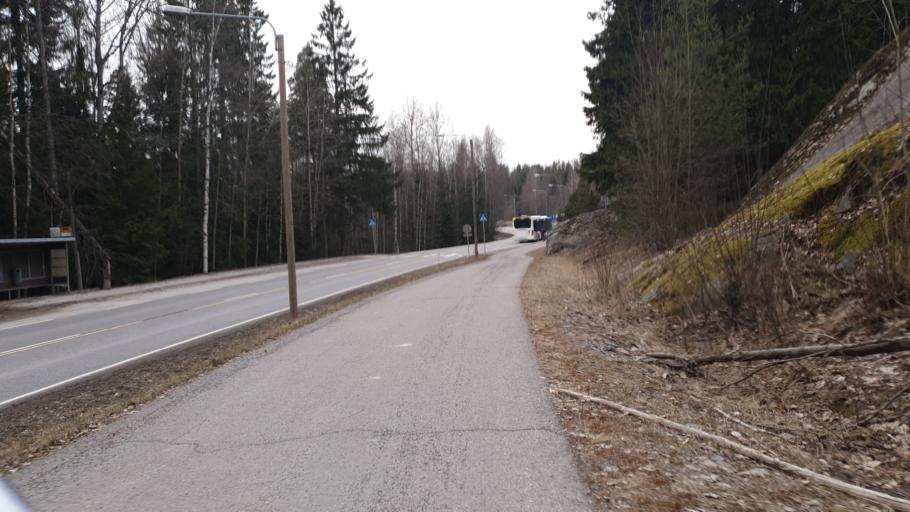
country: FI
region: Uusimaa
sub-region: Helsinki
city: Tuusula
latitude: 60.3458
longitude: 24.9151
